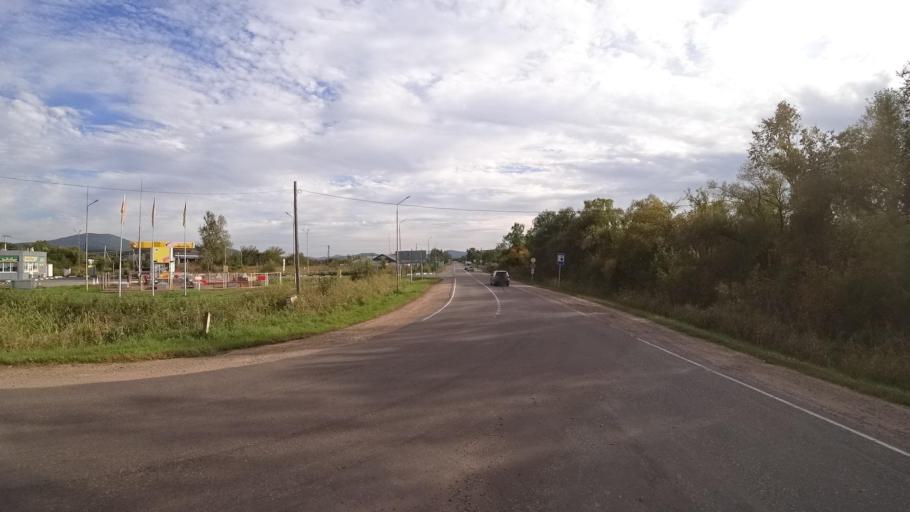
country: RU
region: Primorskiy
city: Dostoyevka
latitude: 44.2949
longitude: 133.4265
